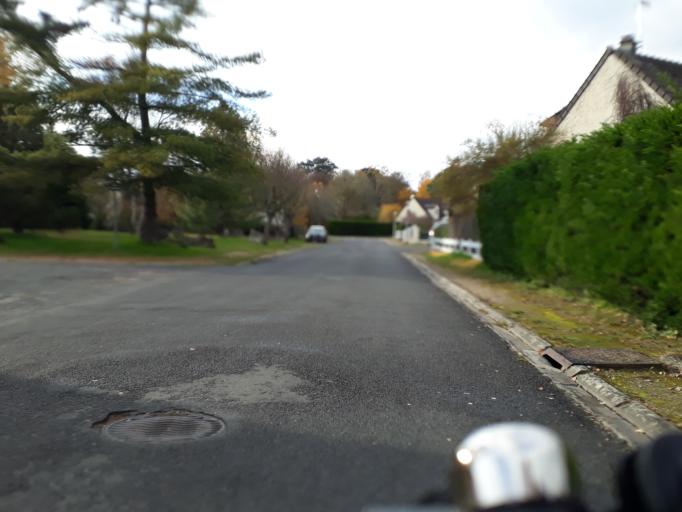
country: FR
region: Ile-de-France
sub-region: Departement de Seine-et-Marne
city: Bois-le-Roi
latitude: 48.4684
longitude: 2.6935
